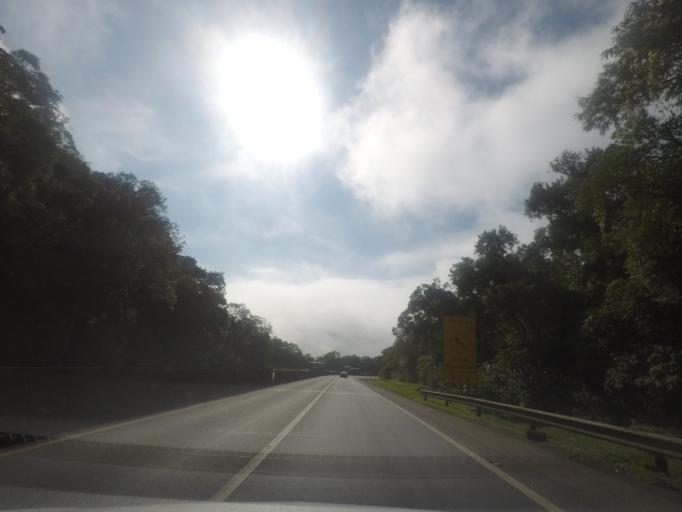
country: BR
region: Parana
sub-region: Piraquara
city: Piraquara
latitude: -25.5929
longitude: -48.8893
